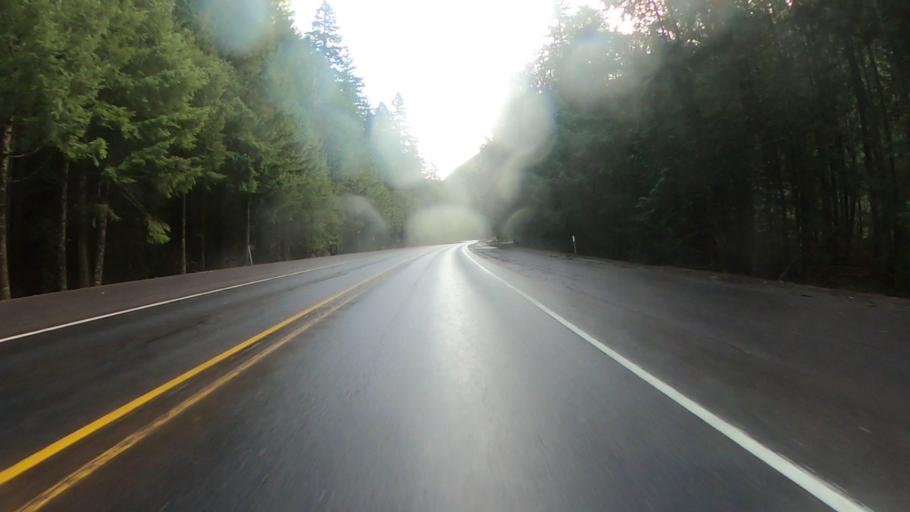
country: US
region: Oregon
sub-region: Lane County
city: Oakridge
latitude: 43.6518
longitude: -122.2150
